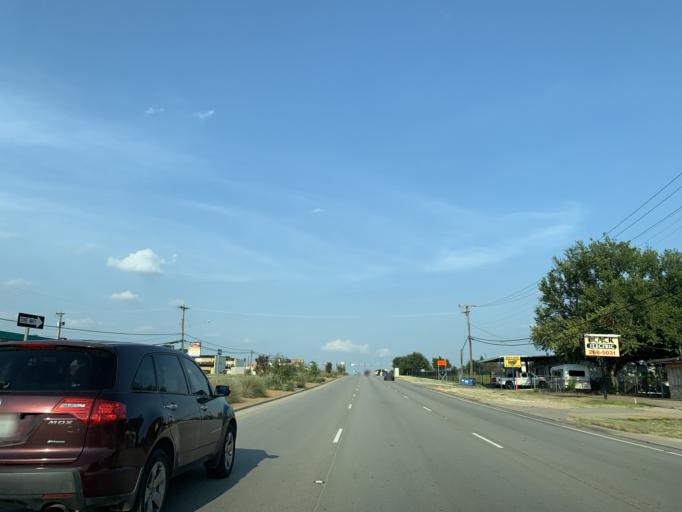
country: US
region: Texas
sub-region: Tarrant County
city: Hurst
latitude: 32.8088
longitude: -97.1658
